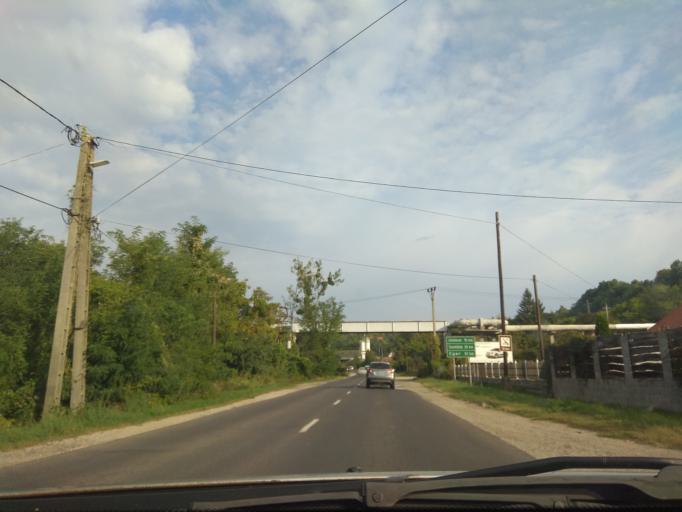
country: HU
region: Borsod-Abauj-Zemplen
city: Miskolc
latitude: 48.0863
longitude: 20.7690
